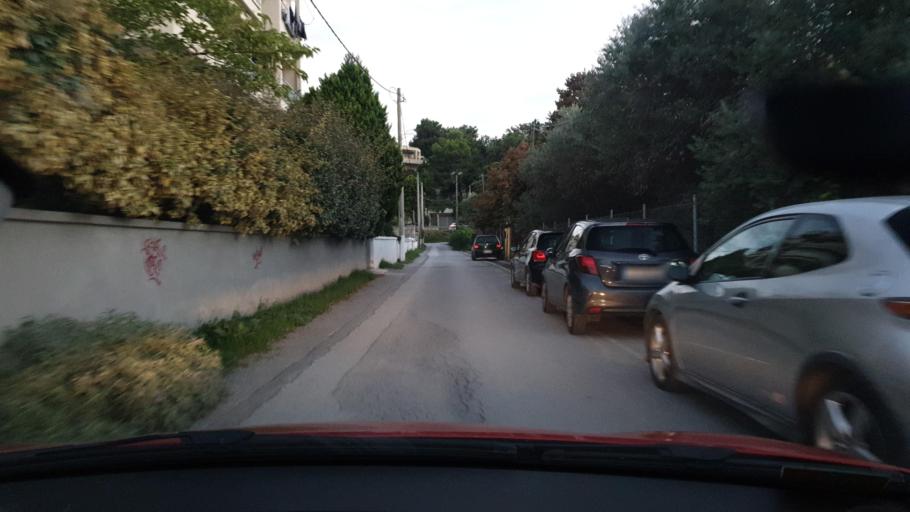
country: GR
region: Central Macedonia
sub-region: Nomos Thessalonikis
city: Neoi Epivates
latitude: 40.5013
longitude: 22.8931
